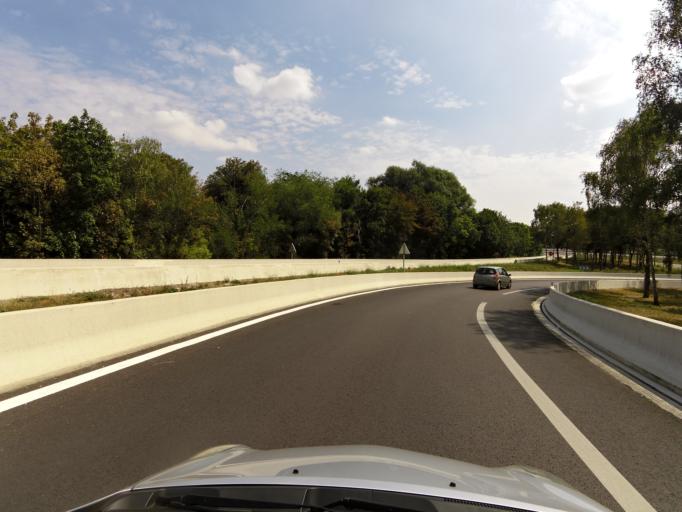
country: FR
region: Champagne-Ardenne
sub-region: Departement de la Marne
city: Reims
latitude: 49.2345
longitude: 4.0416
